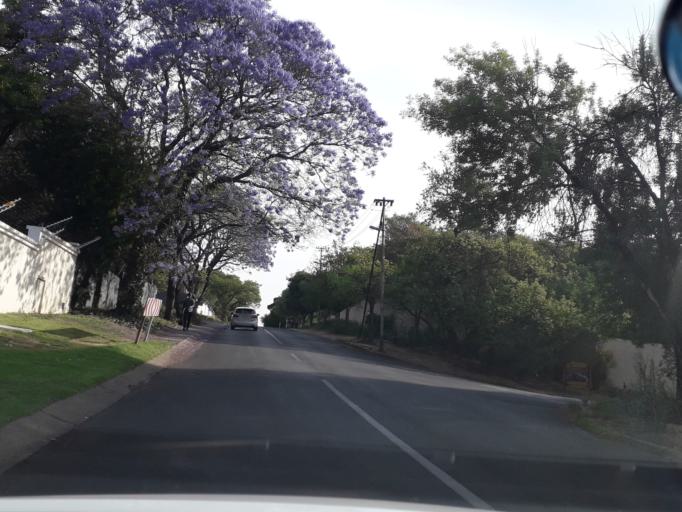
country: ZA
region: Gauteng
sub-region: City of Johannesburg Metropolitan Municipality
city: Diepsloot
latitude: -26.0477
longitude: 28.0077
